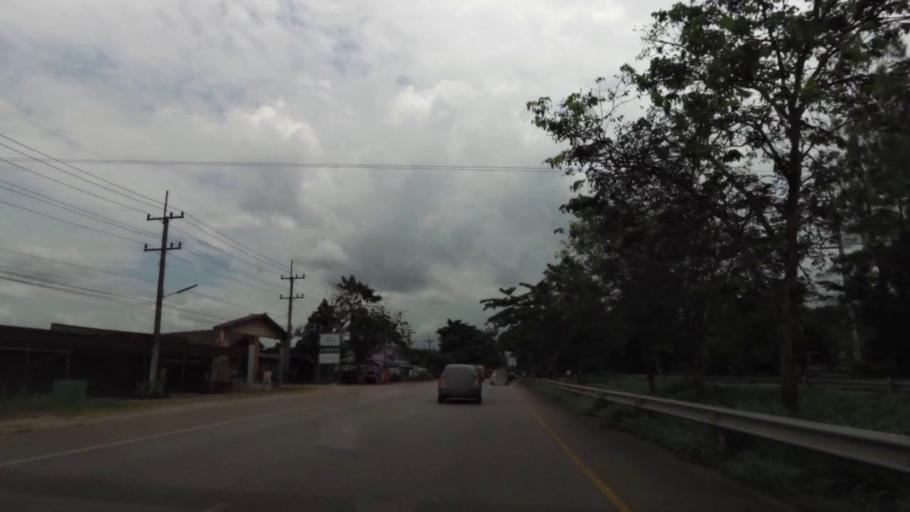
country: TH
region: Rayong
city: Wang Chan
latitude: 12.8844
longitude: 101.5566
